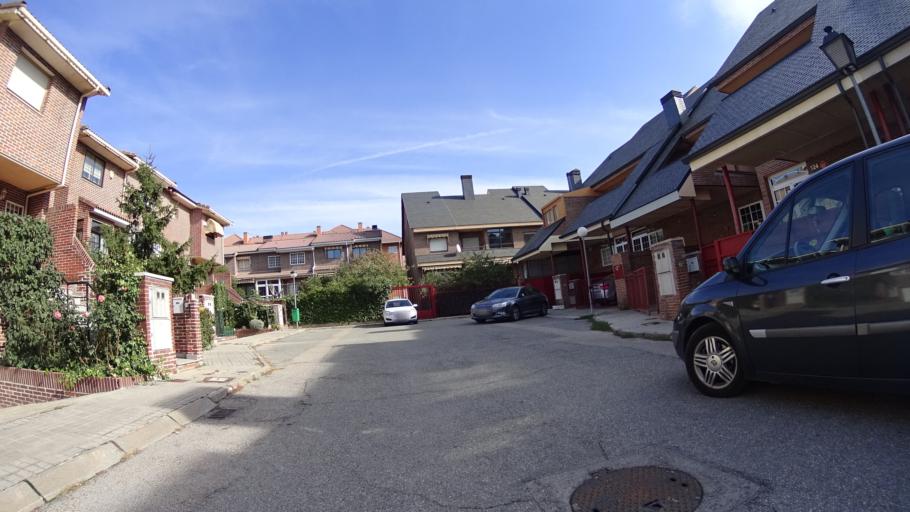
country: ES
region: Madrid
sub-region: Provincia de Madrid
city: Collado-Villalba
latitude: 40.6192
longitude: -4.0168
